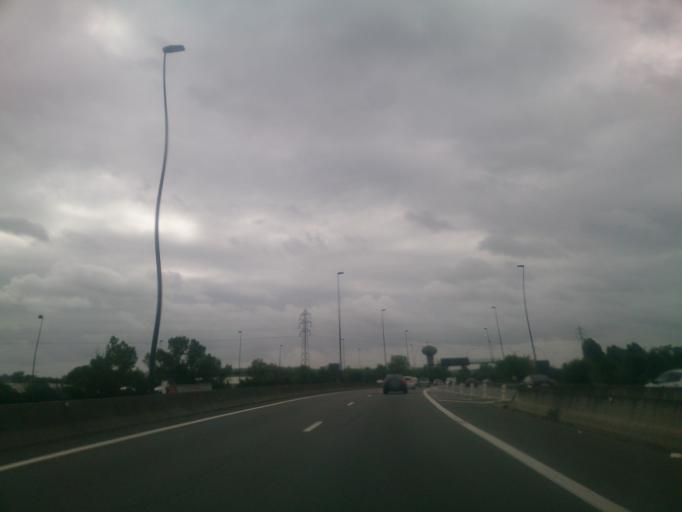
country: FR
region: Midi-Pyrenees
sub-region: Departement de la Haute-Garonne
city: Portet-sur-Garonne
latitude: 43.5661
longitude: 1.4183
